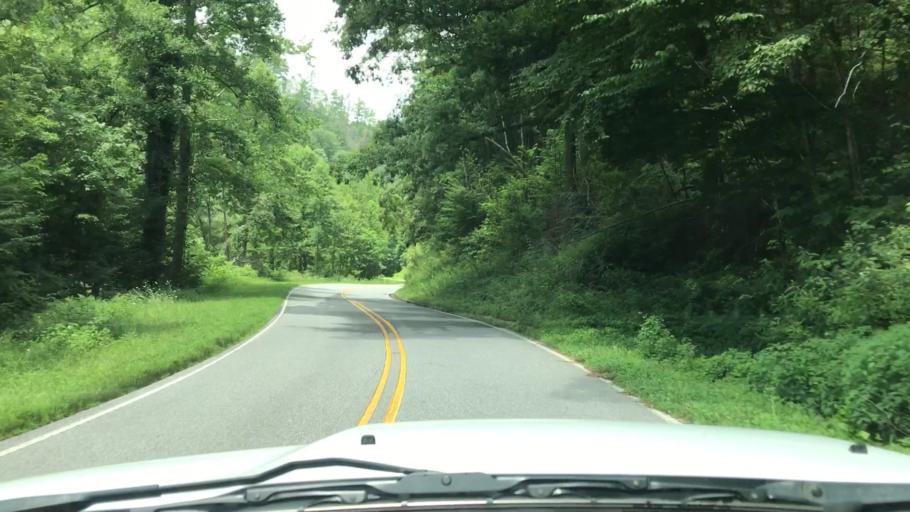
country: US
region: North Carolina
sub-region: Graham County
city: Robbinsville
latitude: 35.4097
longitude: -83.8867
